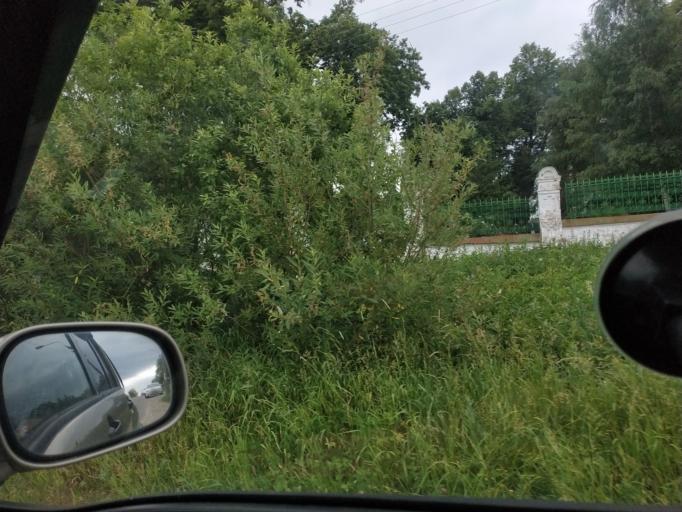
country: RU
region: Moskovskaya
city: Krasnoarmeysk
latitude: 56.0870
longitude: 38.2254
